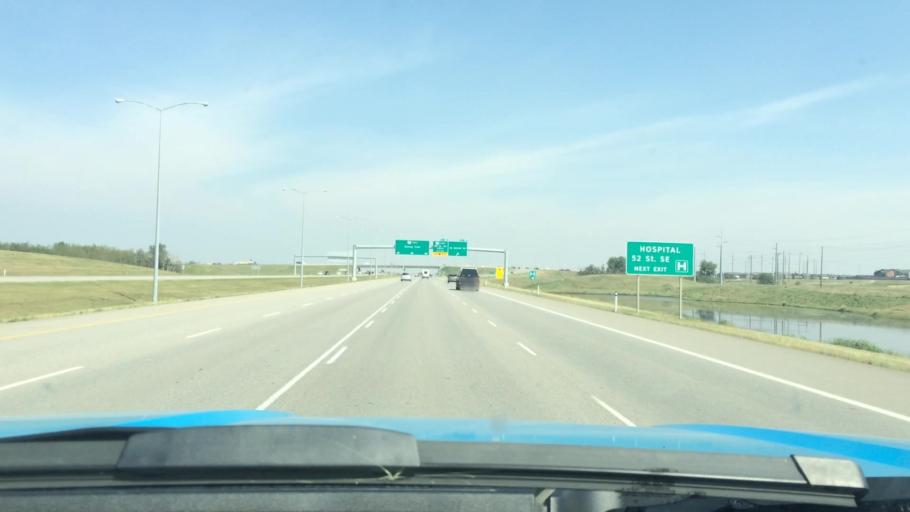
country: CA
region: Alberta
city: Okotoks
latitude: 50.9027
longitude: -113.9592
